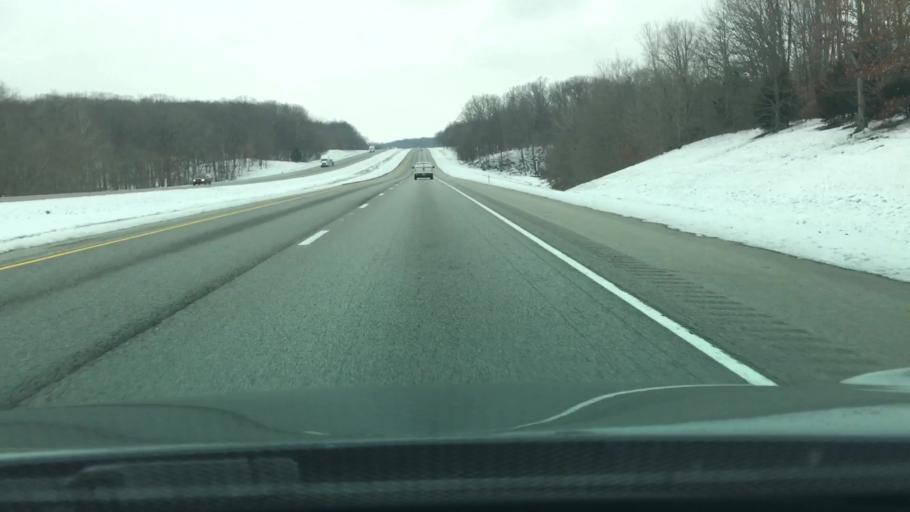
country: US
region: Illinois
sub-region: Clinton County
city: Wamac
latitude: 38.3689
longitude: -89.0920
